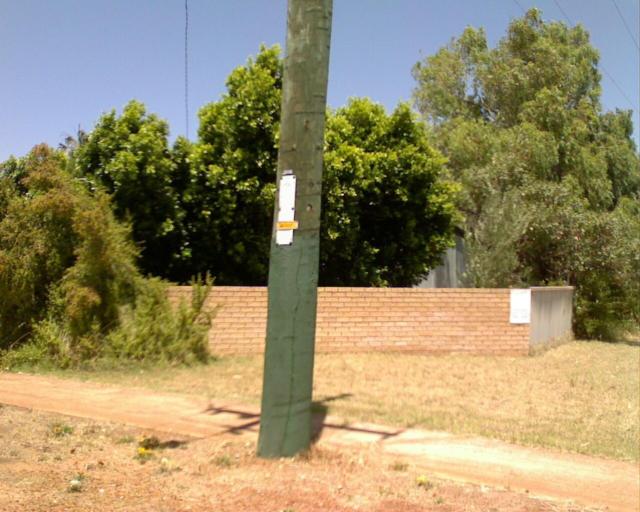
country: AU
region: Western Australia
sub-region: Irwin
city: Dongara
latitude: -29.1930
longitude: 115.4420
